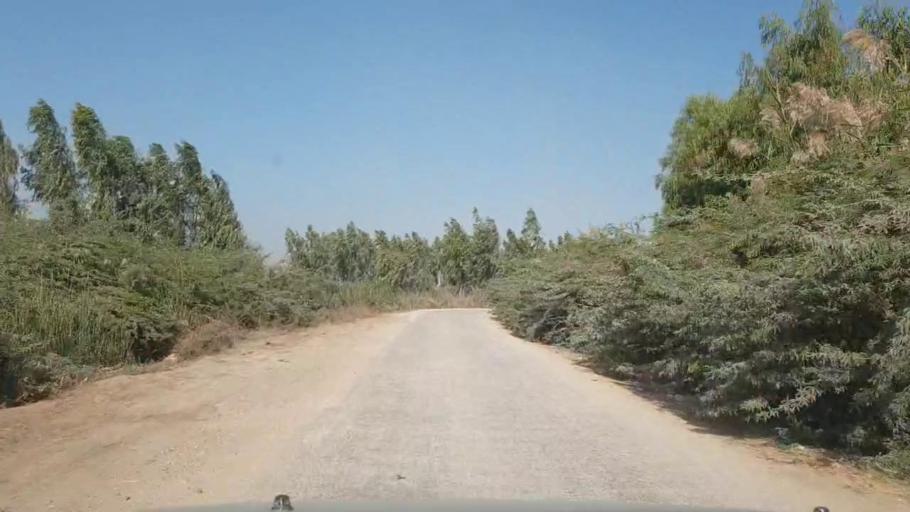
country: PK
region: Sindh
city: Thatta
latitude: 24.7930
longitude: 67.9020
